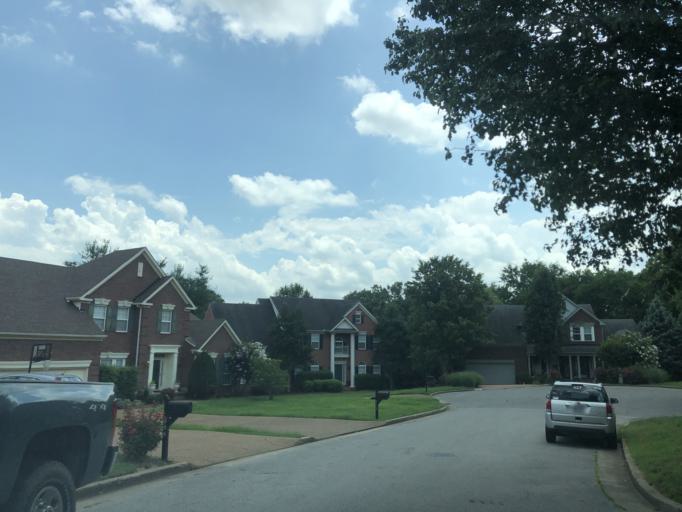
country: US
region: Tennessee
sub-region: Williamson County
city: Brentwood Estates
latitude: 36.0106
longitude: -86.7227
